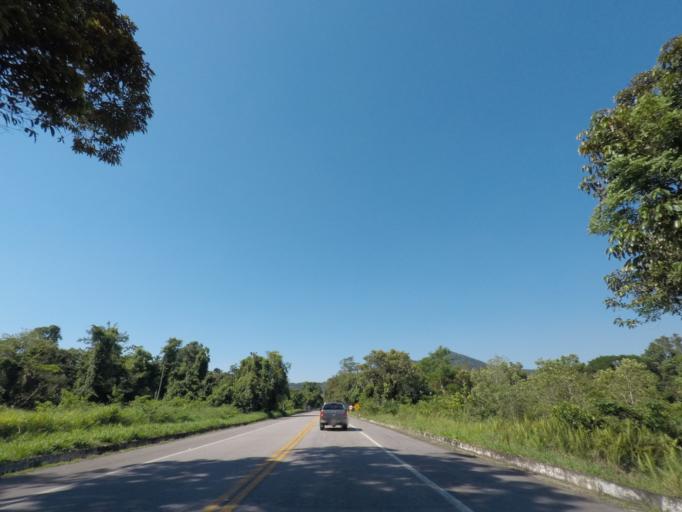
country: BR
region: Sao Paulo
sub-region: Ubatuba
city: Ubatuba
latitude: -23.3369
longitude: -44.9339
